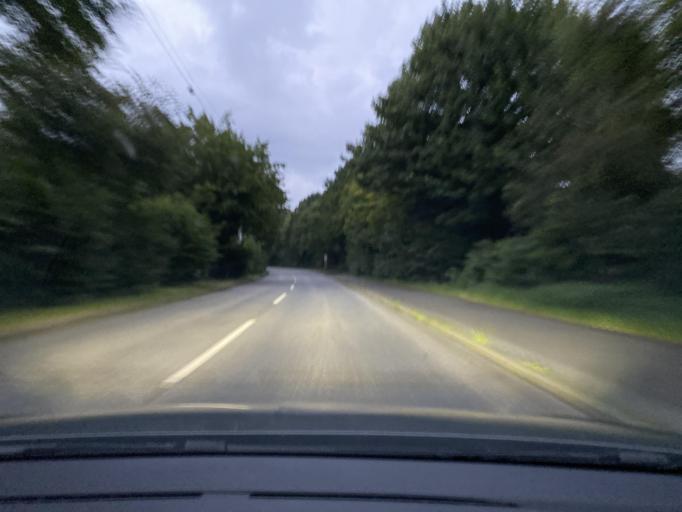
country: DE
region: North Rhine-Westphalia
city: Witten
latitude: 51.4577
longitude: 7.2956
